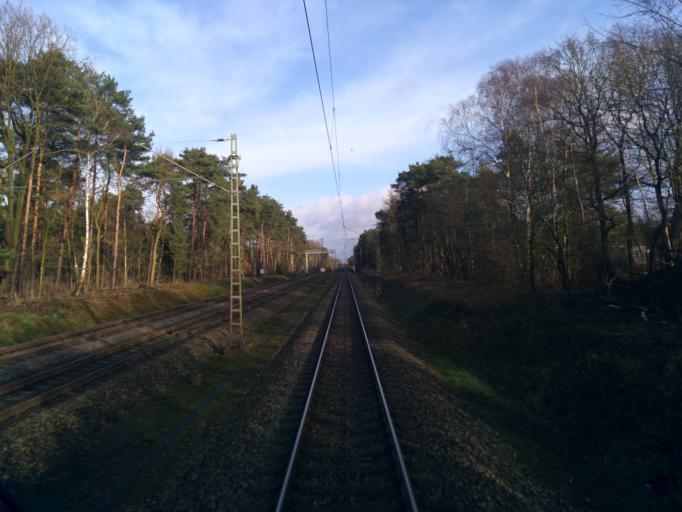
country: DE
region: Lower Saxony
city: Rotenburg
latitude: 53.1284
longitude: 9.4341
